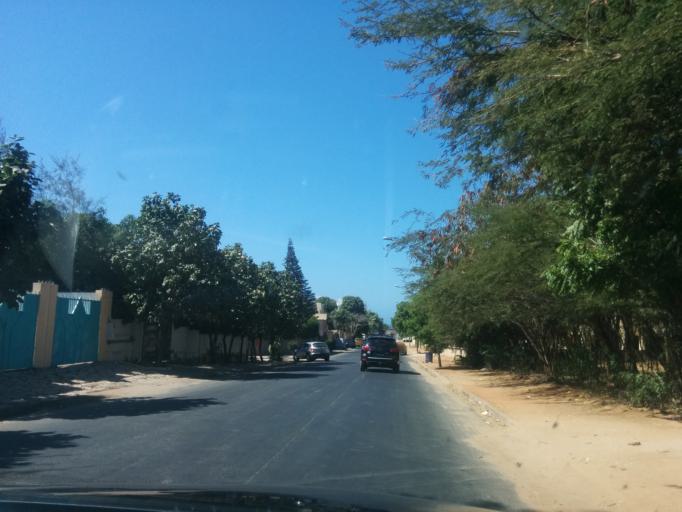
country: SN
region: Dakar
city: Mermoz Boabab
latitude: 14.7094
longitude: -17.4822
